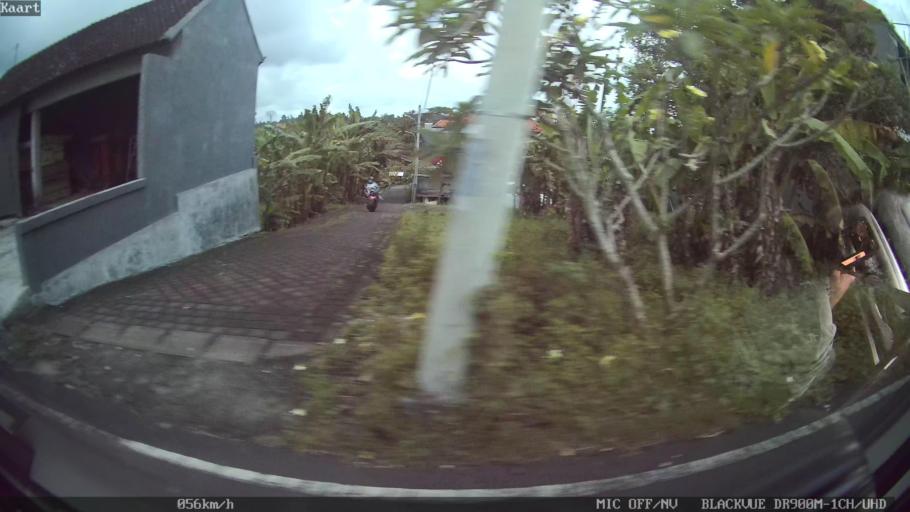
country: ID
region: Bali
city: Banjar Serangan
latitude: -8.5531
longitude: 115.1808
